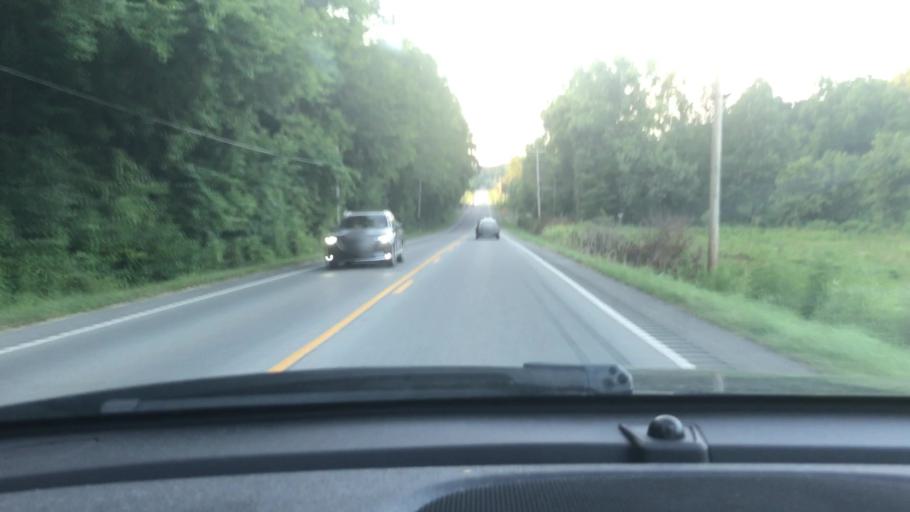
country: US
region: Tennessee
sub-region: Dickson County
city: Charlotte
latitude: 36.1262
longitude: -87.3600
